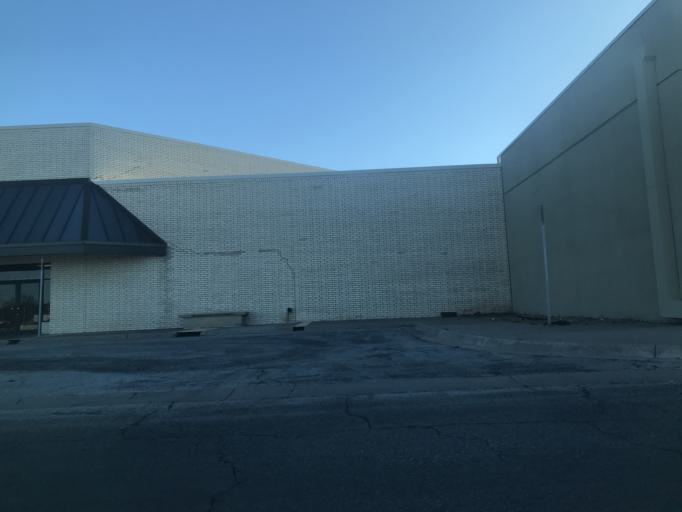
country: US
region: Texas
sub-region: Tom Green County
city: San Angelo
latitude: 31.4279
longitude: -100.4972
